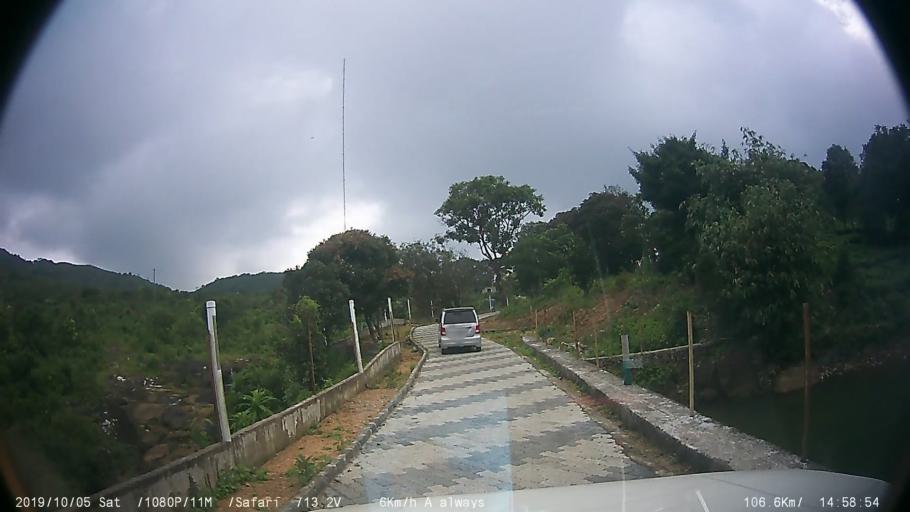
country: IN
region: Kerala
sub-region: Kottayam
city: Erattupetta
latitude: 9.6201
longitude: 76.9343
